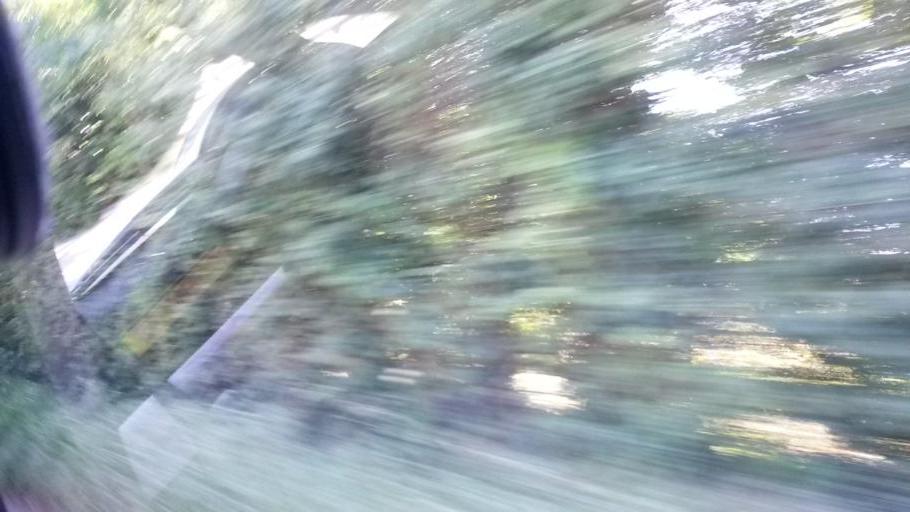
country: IE
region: Leinster
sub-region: An Mhi
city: Ashbourne
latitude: 53.5266
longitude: -6.2988
